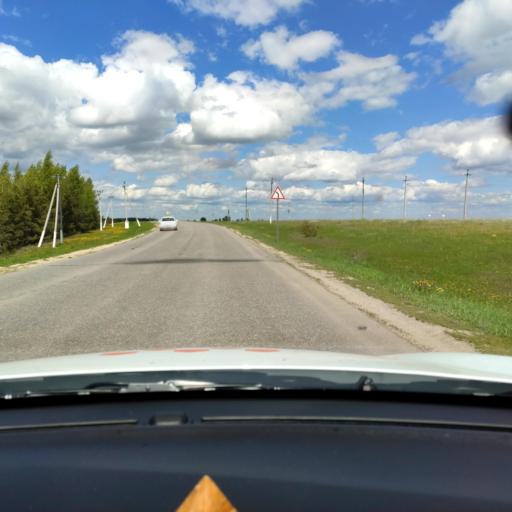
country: RU
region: Tatarstan
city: Verkhniy Uslon
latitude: 55.6189
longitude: 48.8791
